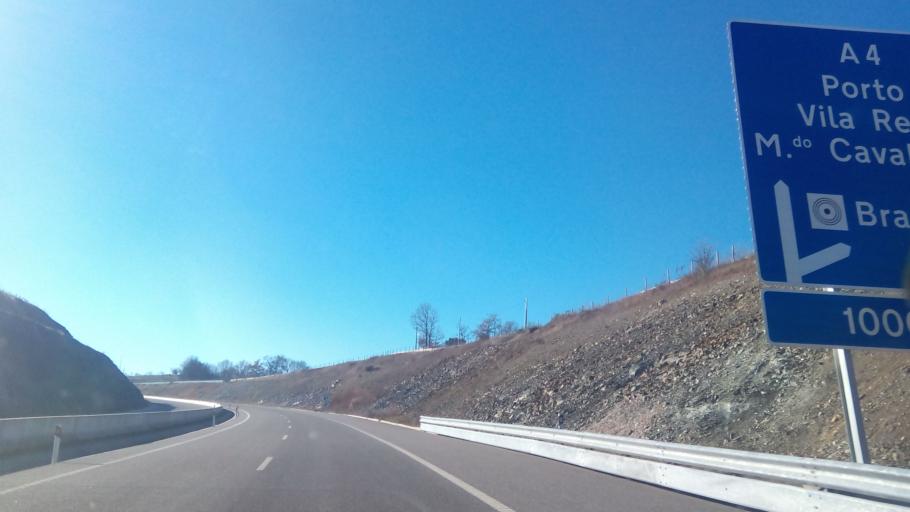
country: PT
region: Braganca
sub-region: Braganca Municipality
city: Braganca
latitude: 41.7735
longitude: -6.7553
